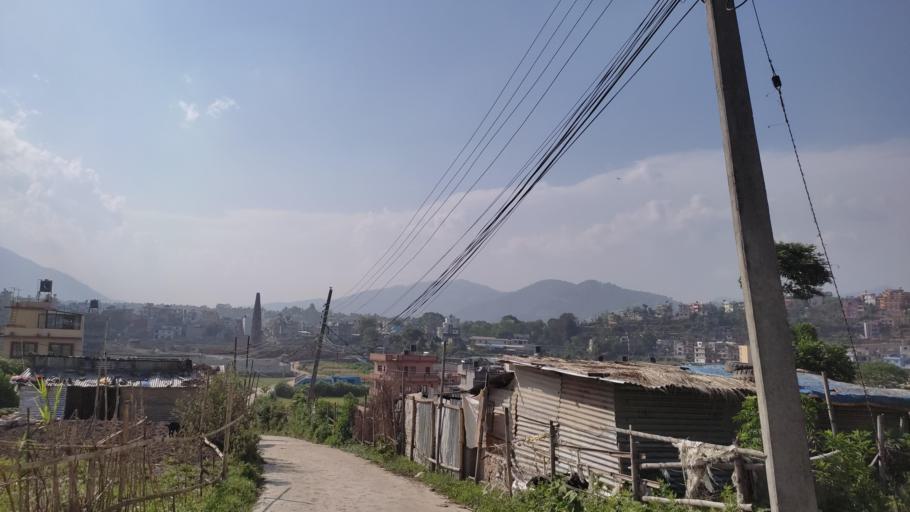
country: NP
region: Central Region
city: Kirtipur
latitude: 27.6783
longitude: 85.2651
